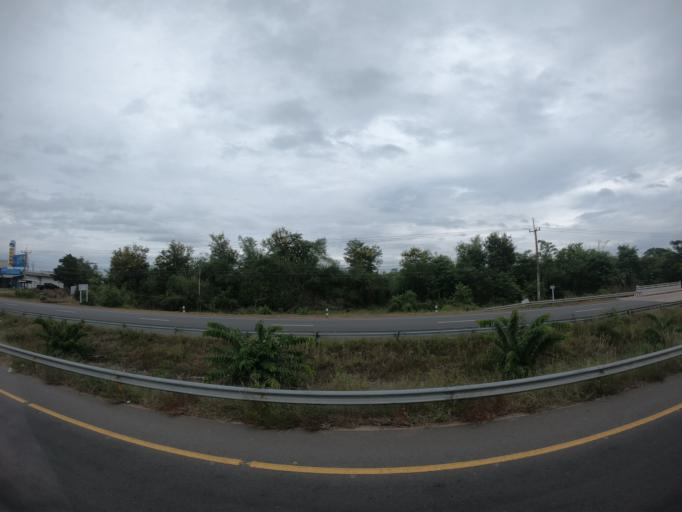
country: TH
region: Roi Et
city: Changhan
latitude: 16.1171
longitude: 103.4922
